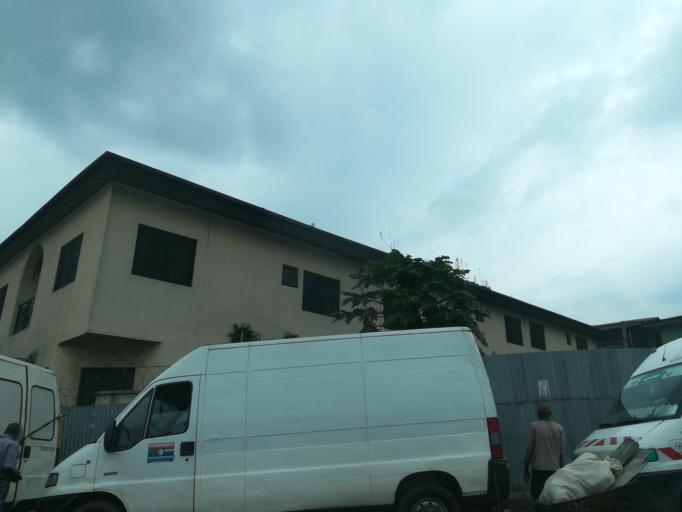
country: NG
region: Lagos
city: Ojota
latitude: 6.6119
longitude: 3.3962
